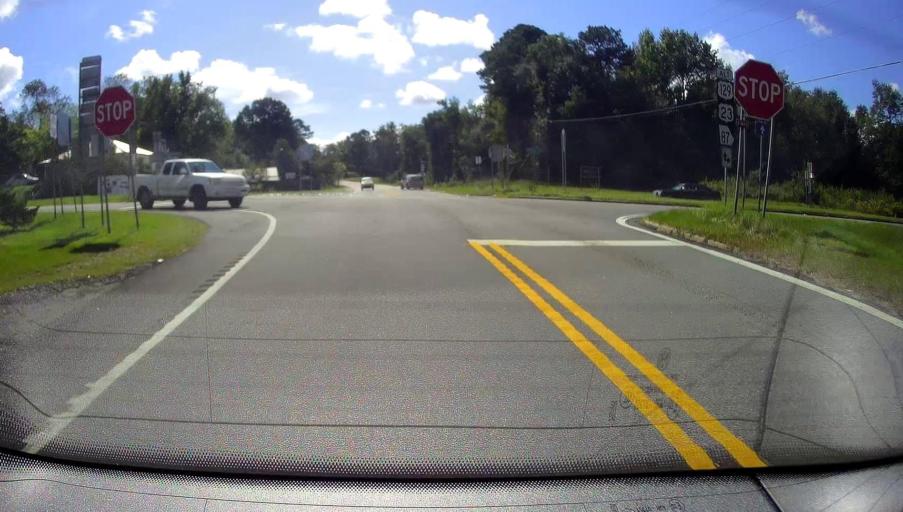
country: US
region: Georgia
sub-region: Bibb County
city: Macon
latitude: 32.8387
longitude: -83.5753
